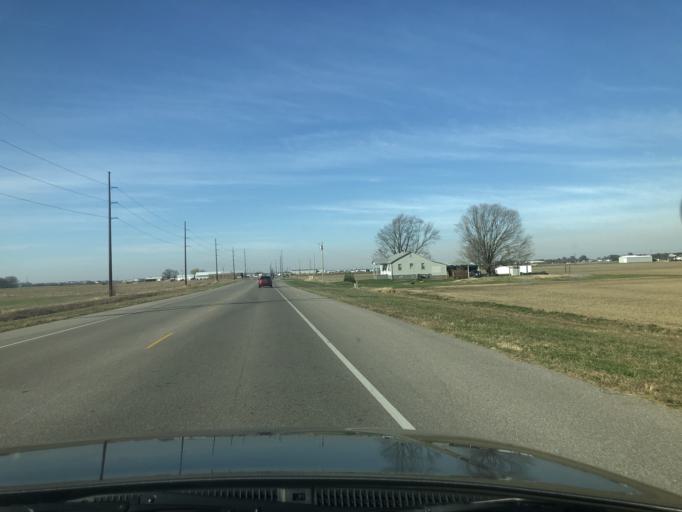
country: US
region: Indiana
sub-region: Warrick County
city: Newburgh
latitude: 37.9911
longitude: -87.4349
